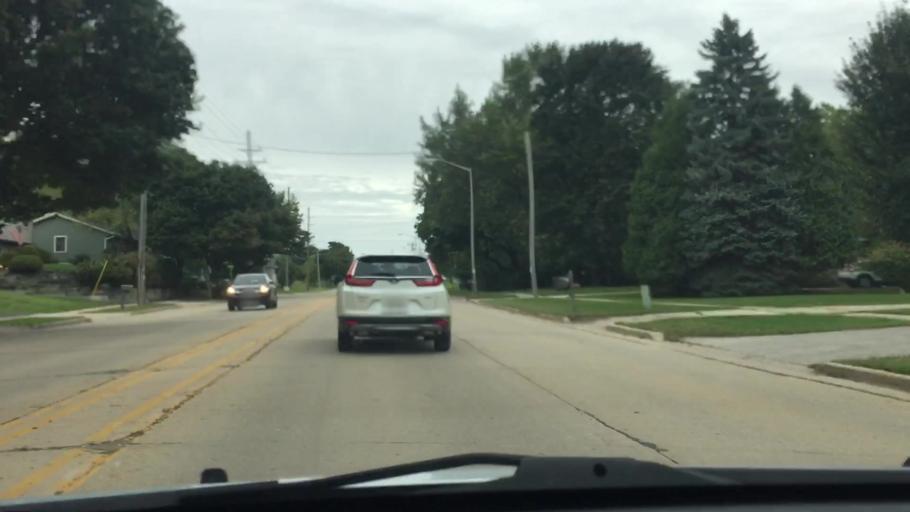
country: US
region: Wisconsin
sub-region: Waukesha County
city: Waukesha
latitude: 43.0271
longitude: -88.2424
